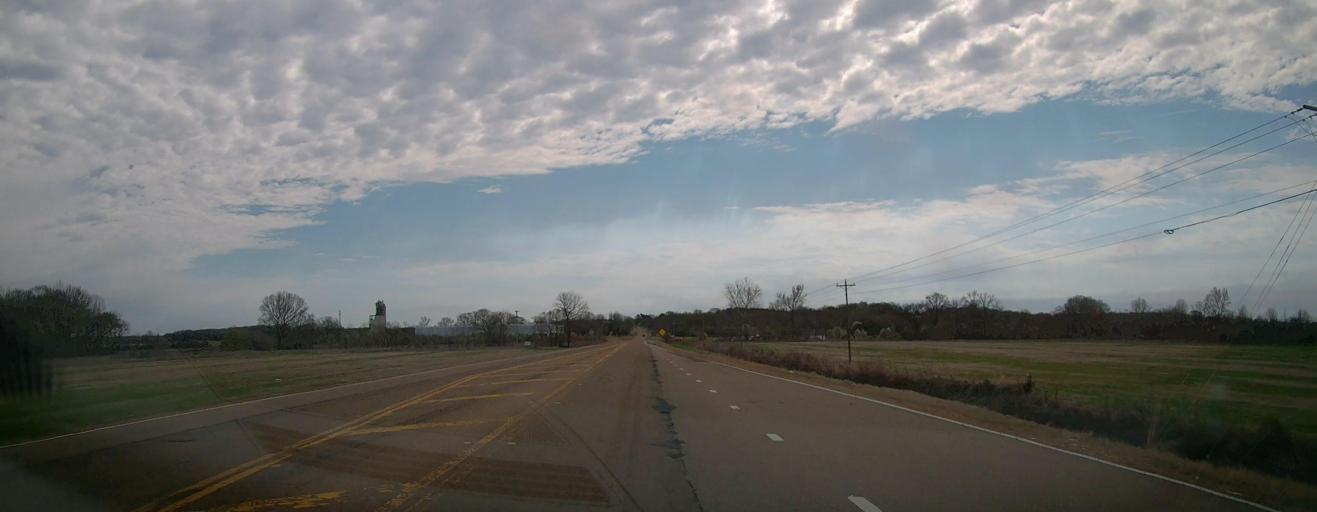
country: US
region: Mississippi
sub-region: Marshall County
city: Byhalia
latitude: 34.8671
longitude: -89.6662
